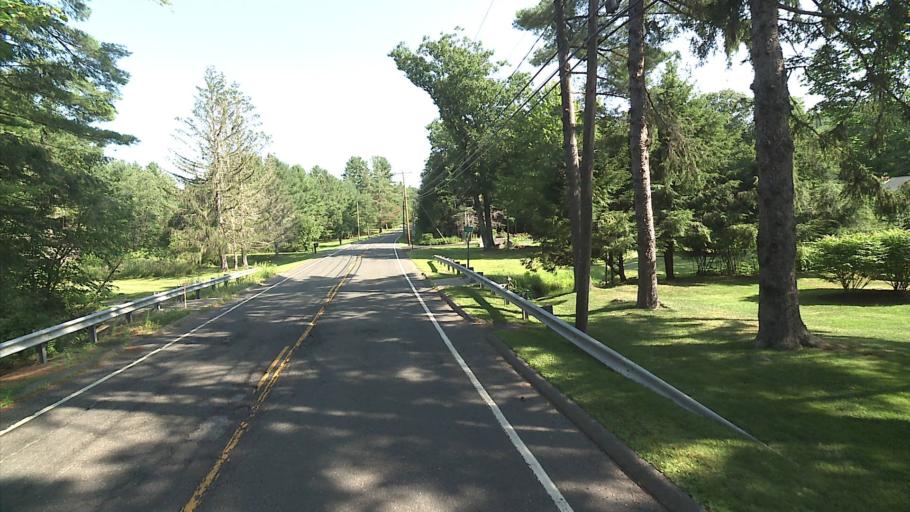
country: US
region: Connecticut
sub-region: Litchfield County
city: Winsted
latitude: 41.9615
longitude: -73.1031
